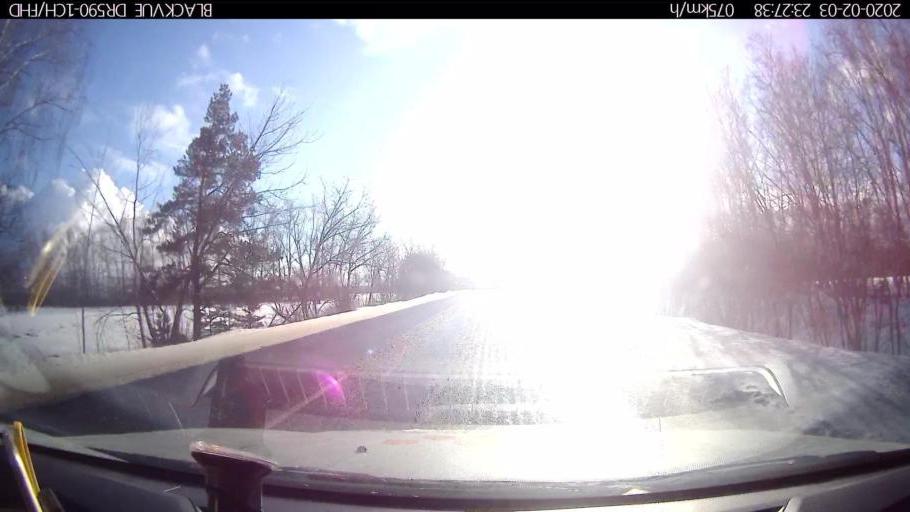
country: RU
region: Nizjnij Novgorod
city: Kstovo
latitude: 55.9801
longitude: 44.2114
